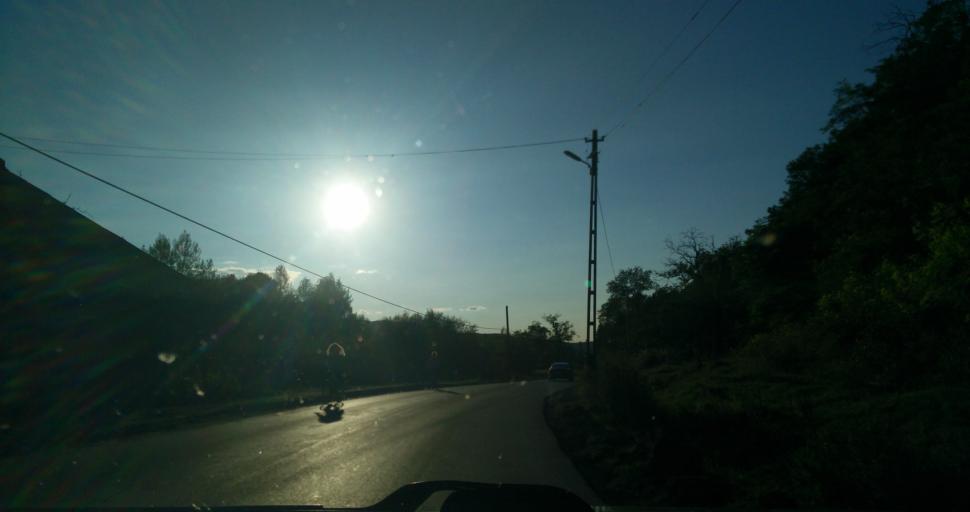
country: RO
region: Bihor
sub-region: Oras Nucet
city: Nucet
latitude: 46.4833
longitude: 22.5713
